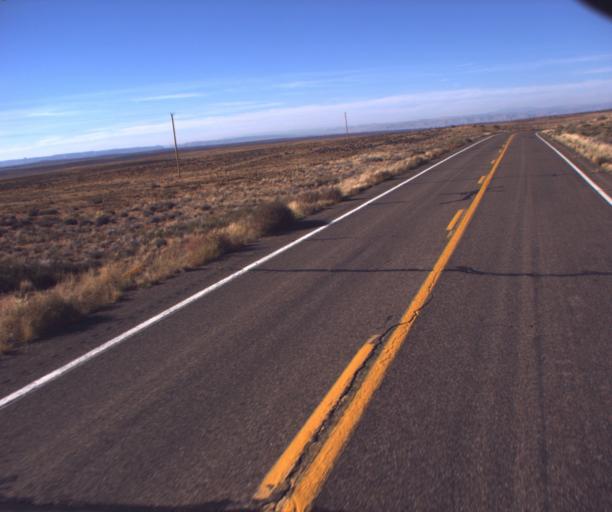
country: US
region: Arizona
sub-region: Coconino County
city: LeChee
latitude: 36.7313
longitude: -111.2831
